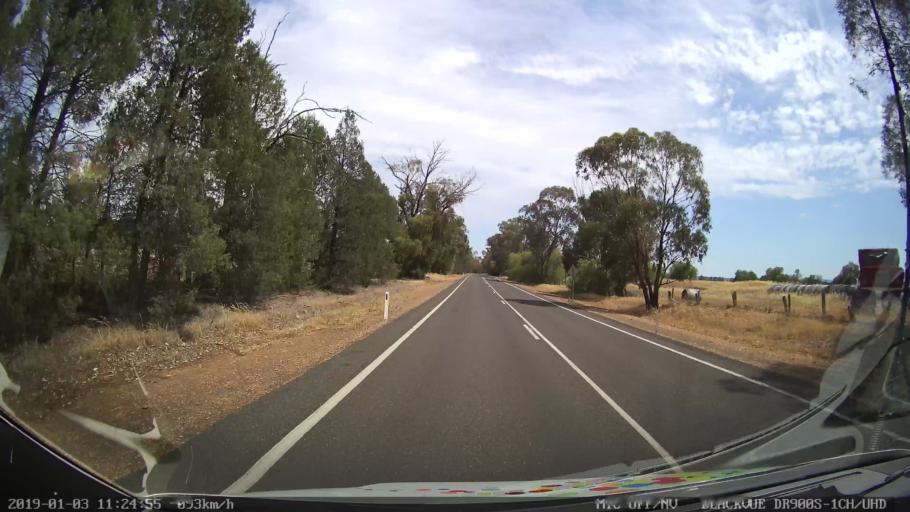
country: AU
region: New South Wales
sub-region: Weddin
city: Grenfell
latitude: -34.0453
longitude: 148.2320
